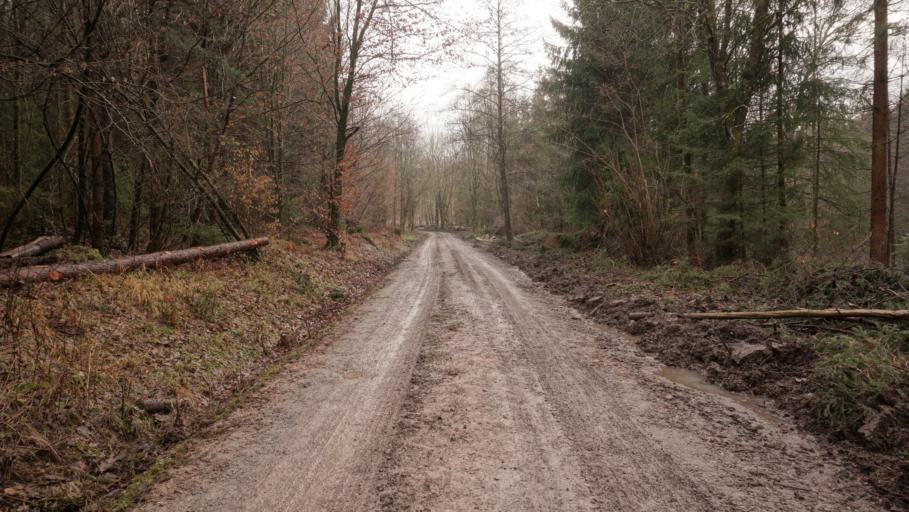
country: DE
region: Baden-Wuerttemberg
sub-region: Karlsruhe Region
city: Reichartshausen
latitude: 49.4073
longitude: 8.9533
